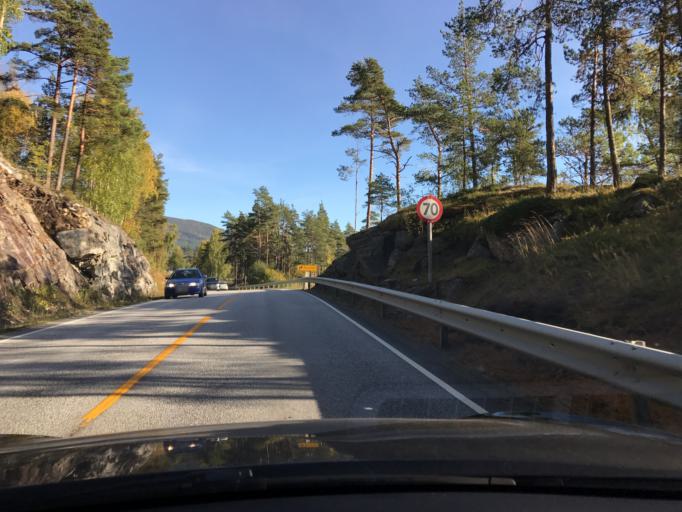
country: NO
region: Sogn og Fjordane
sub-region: Sogndal
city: Sogndalsfjora
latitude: 61.2068
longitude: 7.1638
